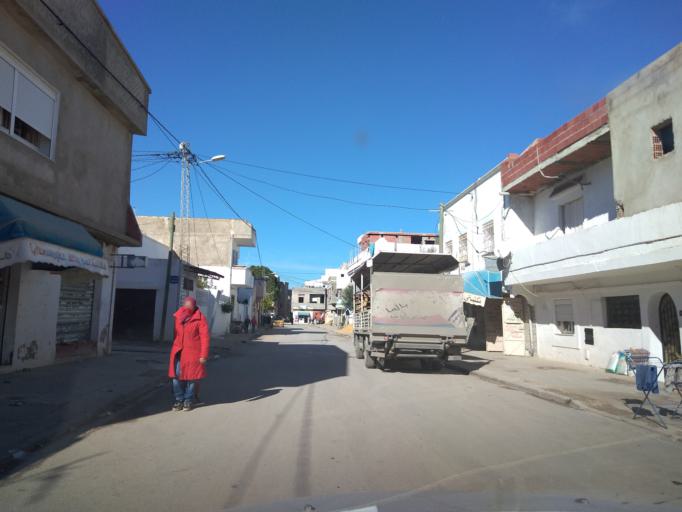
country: TN
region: Manouba
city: Manouba
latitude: 36.7992
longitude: 10.0891
